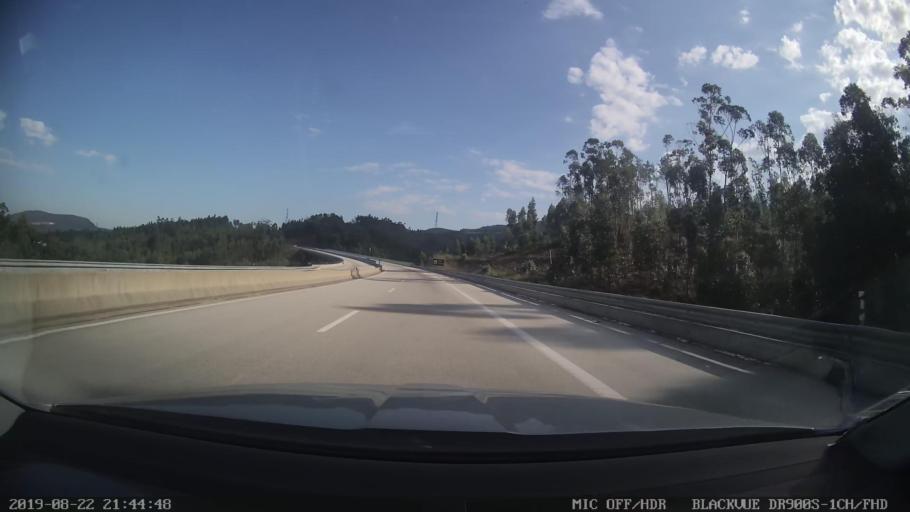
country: PT
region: Coimbra
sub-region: Penela
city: Penela
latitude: 39.9582
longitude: -8.3500
